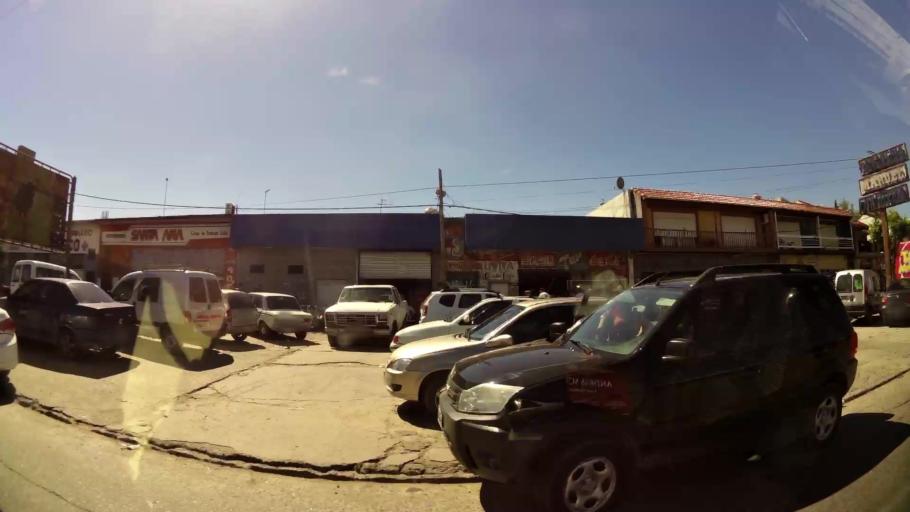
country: AR
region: Buenos Aires
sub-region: Partido de Almirante Brown
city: Adrogue
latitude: -34.7556
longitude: -58.3497
